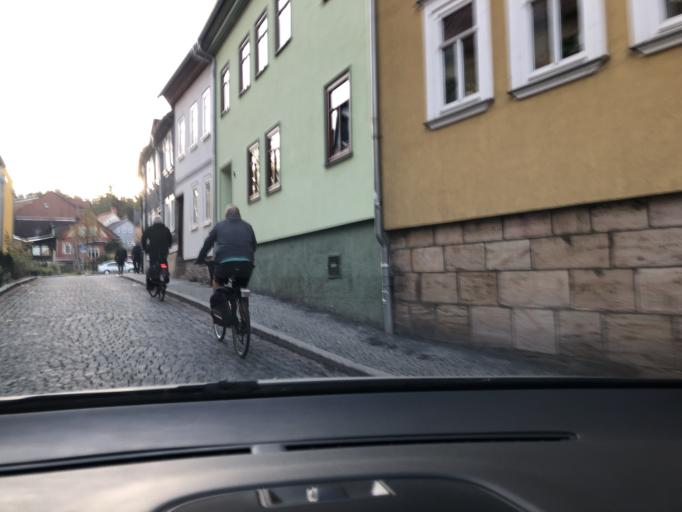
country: DE
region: Thuringia
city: Ilmenau
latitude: 50.6864
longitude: 10.9127
